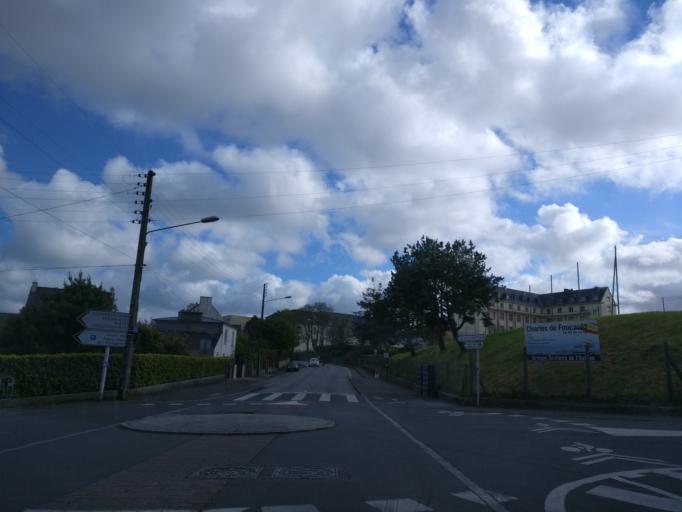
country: FR
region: Brittany
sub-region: Departement du Finistere
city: Brest
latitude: 48.4050
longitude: -4.4577
